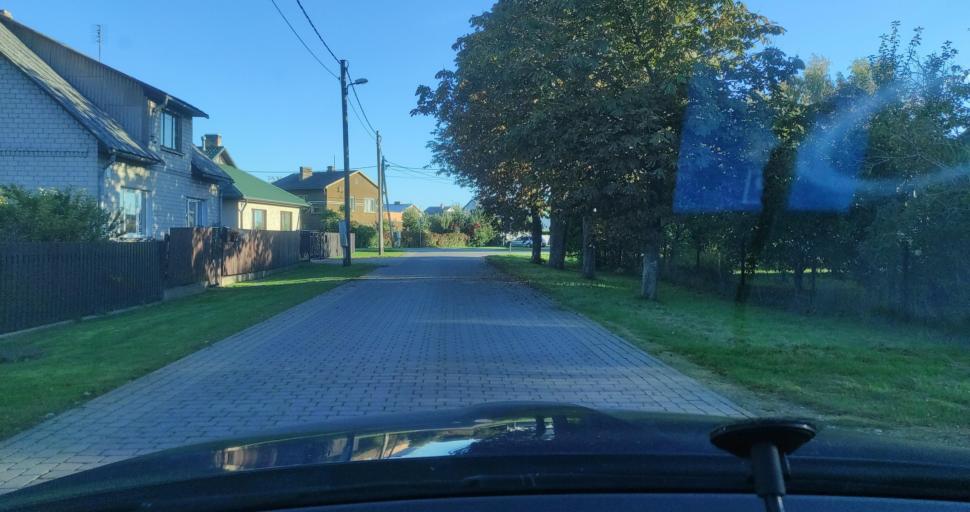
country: LV
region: Ventspils
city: Ventspils
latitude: 57.3743
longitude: 21.5772
